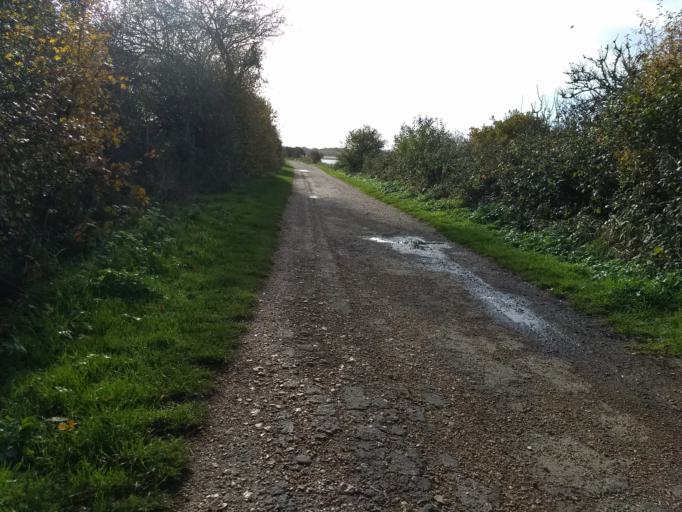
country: GB
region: England
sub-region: Isle of Wight
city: Yarmouth
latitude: 50.6998
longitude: -1.4970
